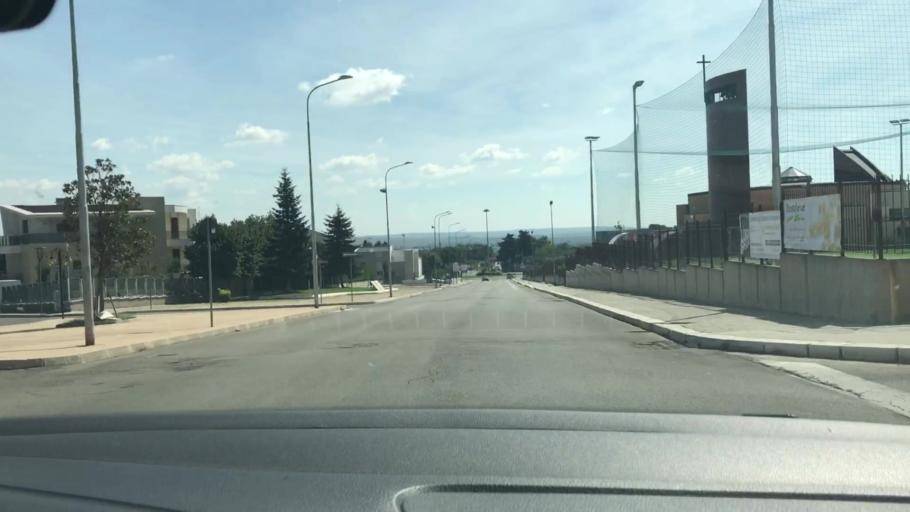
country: IT
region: Apulia
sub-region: Provincia di Bari
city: Altamura
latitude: 40.8262
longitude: 16.5638
